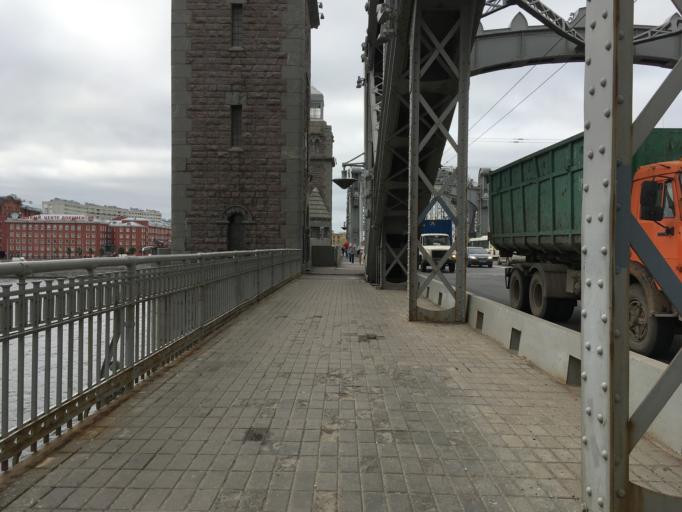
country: RU
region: St.-Petersburg
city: Centralniy
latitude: 59.9425
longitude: 30.4024
